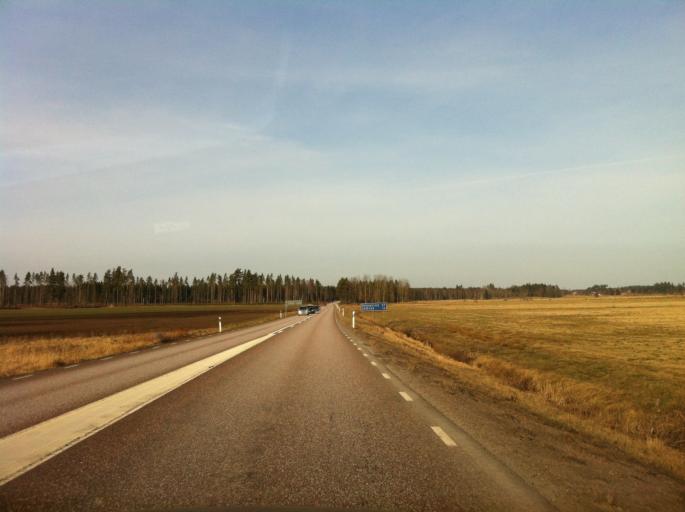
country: SE
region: Vaestra Goetaland
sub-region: Skovde Kommun
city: Skultorp
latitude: 58.2556
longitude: 13.8129
